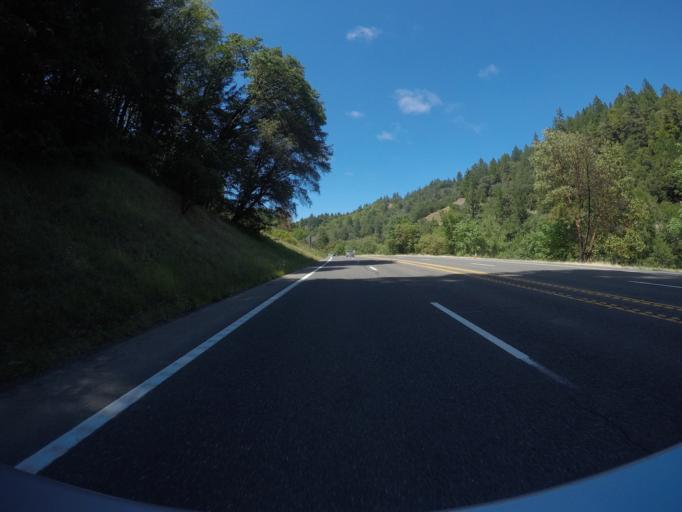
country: US
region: California
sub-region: Mendocino County
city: Brooktrails
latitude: 39.5594
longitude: -123.4329
